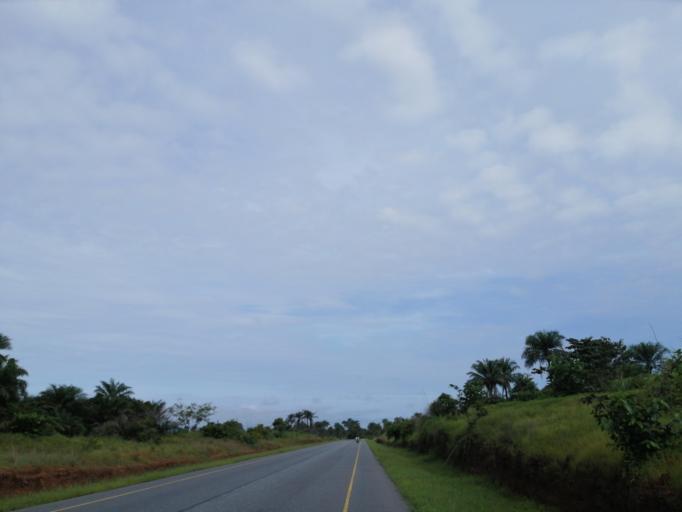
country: SL
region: Northern Province
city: Port Loko
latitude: 8.7697
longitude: -12.8770
